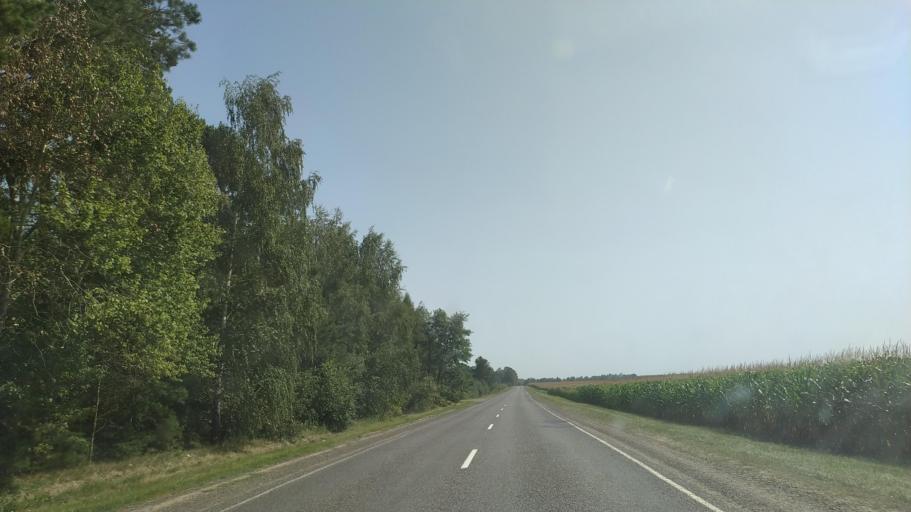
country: BY
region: Brest
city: Byaroza
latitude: 52.4038
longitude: 25.0010
